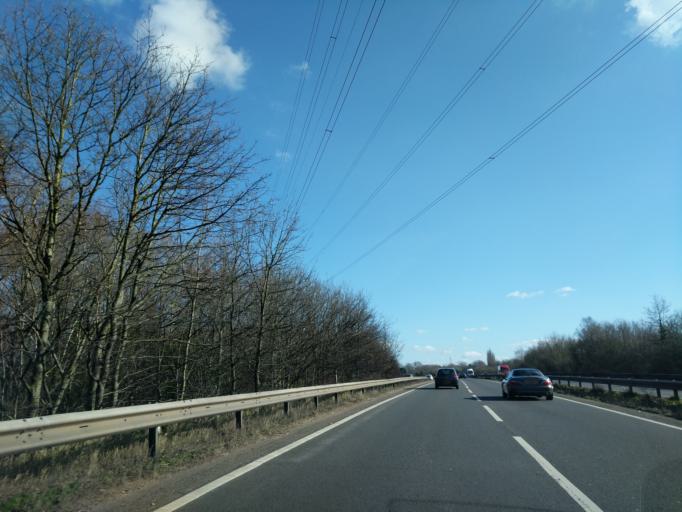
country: GB
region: England
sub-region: Surrey
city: Guildford
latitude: 51.2496
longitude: -0.5747
